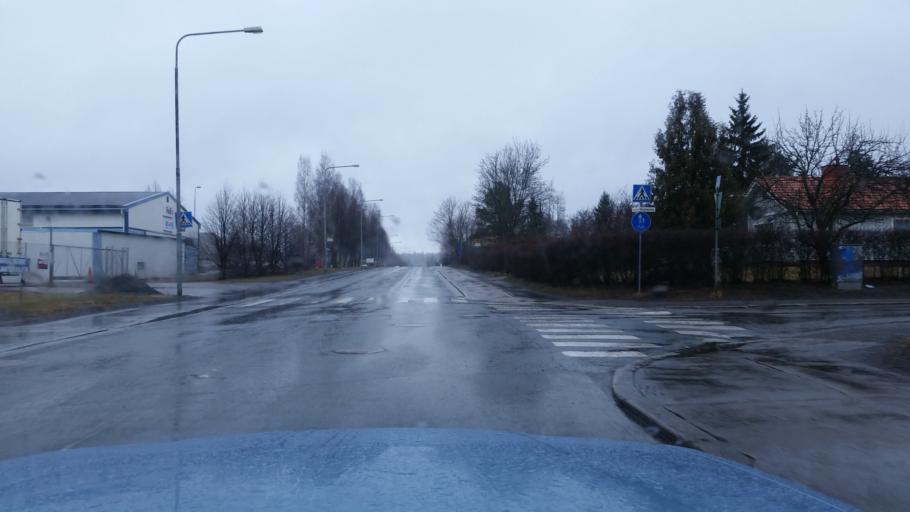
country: FI
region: Pirkanmaa
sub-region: Tampere
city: Tampere
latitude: 61.4769
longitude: 23.7981
